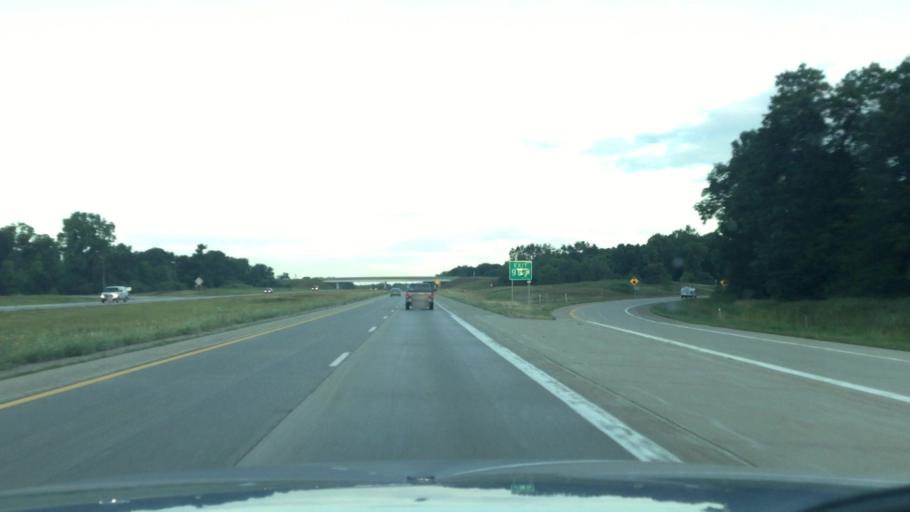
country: US
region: Michigan
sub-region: Ingham County
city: Haslett
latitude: 42.8017
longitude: -84.3427
